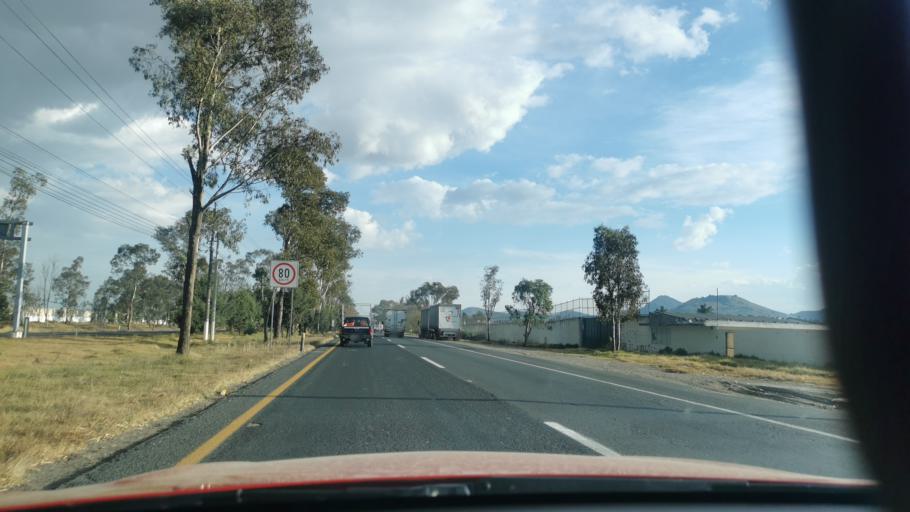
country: MX
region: Mexico
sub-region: Toluca
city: Colonia Aviacion Autopan
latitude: 19.3730
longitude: -99.6980
